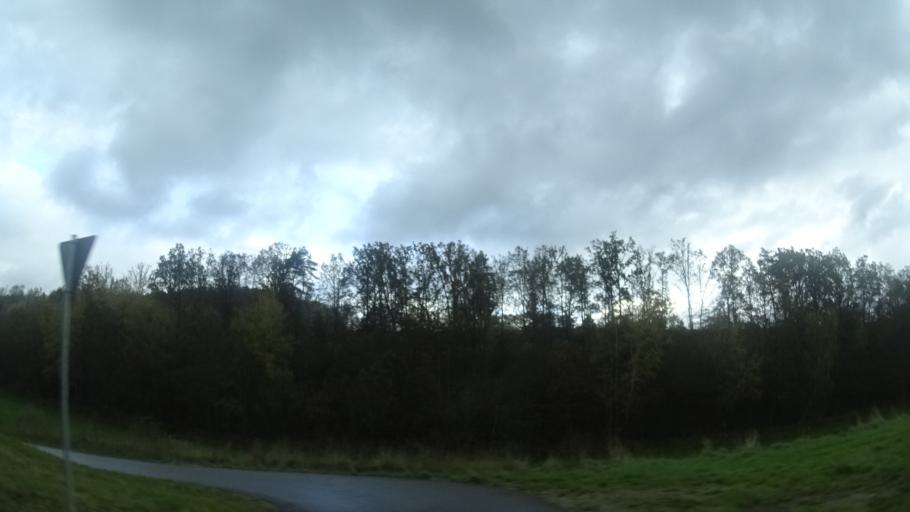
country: DE
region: Bavaria
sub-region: Regierungsbezirk Unterfranken
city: Hohenroth
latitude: 50.3544
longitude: 10.1178
